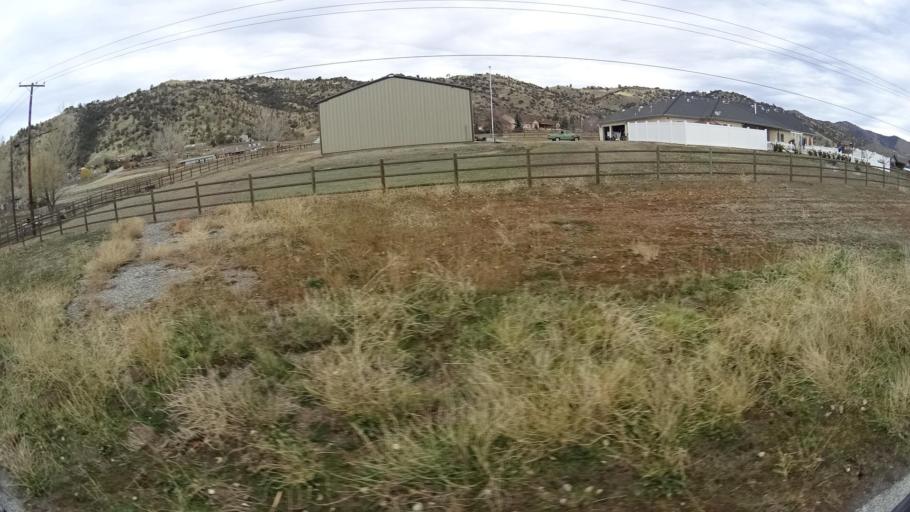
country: US
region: California
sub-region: Kern County
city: Bear Valley Springs
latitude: 35.1231
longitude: -118.6213
